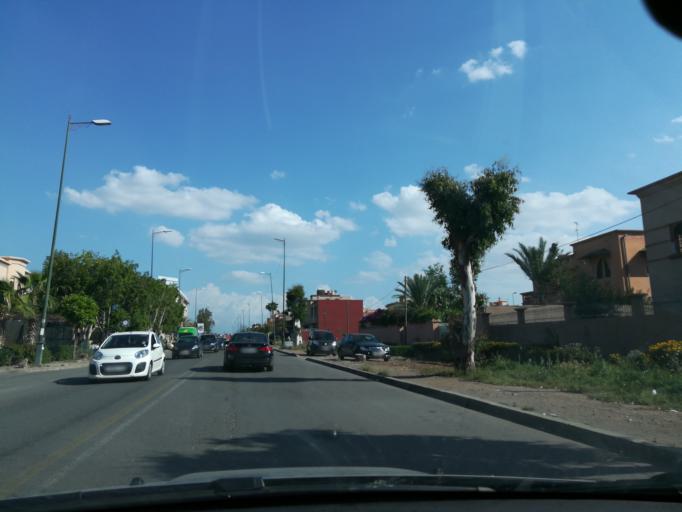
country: MA
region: Marrakech-Tensift-Al Haouz
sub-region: Marrakech
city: Marrakesh
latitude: 31.6507
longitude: -8.0493
